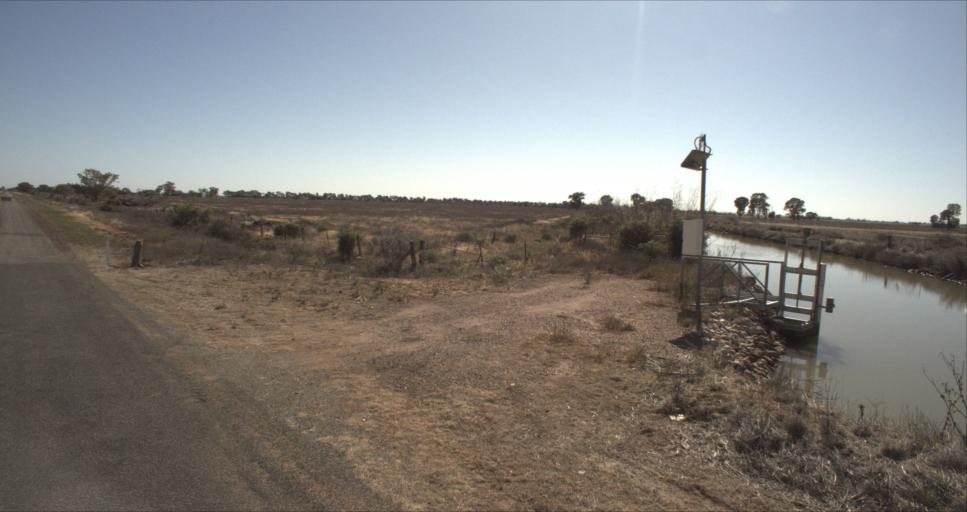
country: AU
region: New South Wales
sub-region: Leeton
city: Leeton
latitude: -34.5882
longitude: 146.2602
